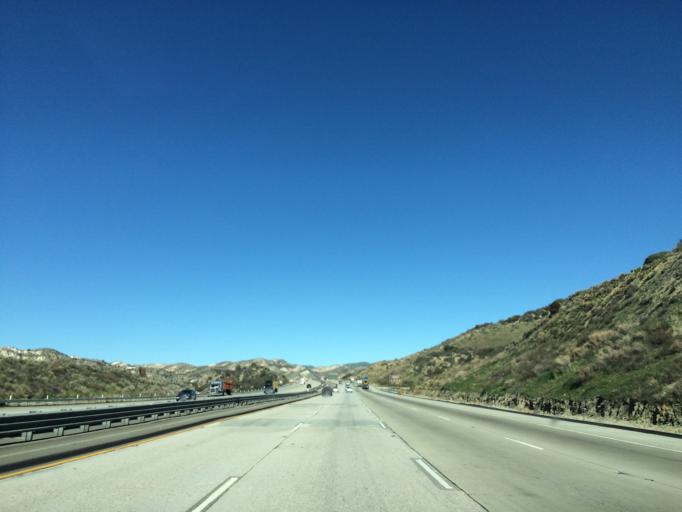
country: US
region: California
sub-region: Kern County
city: Lebec
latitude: 34.6984
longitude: -118.7922
